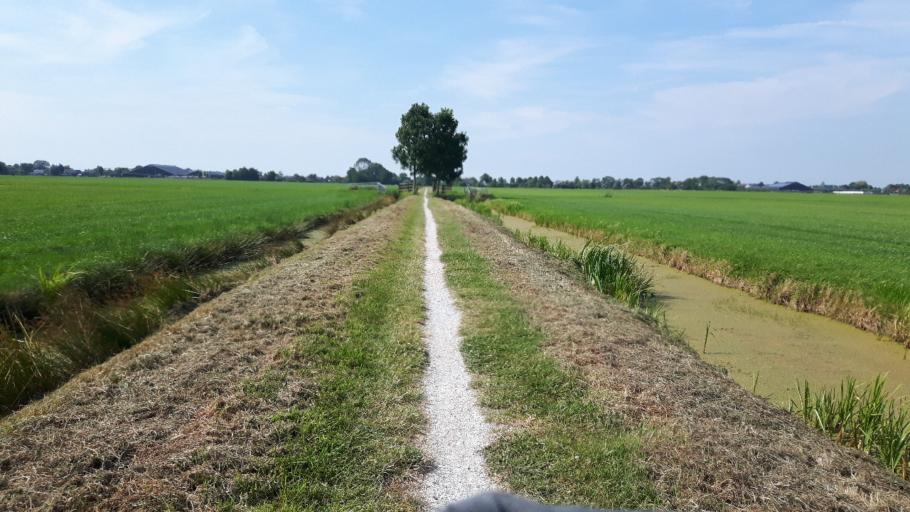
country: NL
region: Utrecht
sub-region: Gemeente Oudewater
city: Oudewater
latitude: 51.9805
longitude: 4.8881
